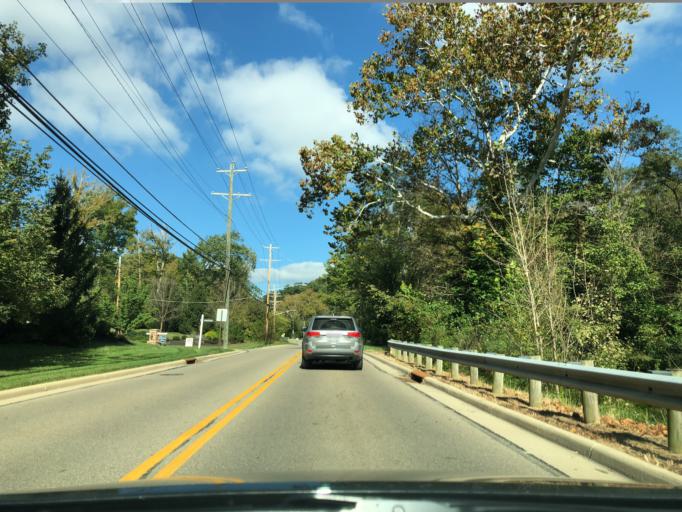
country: US
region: Ohio
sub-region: Hamilton County
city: Loveland
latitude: 39.2714
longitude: -84.2529
